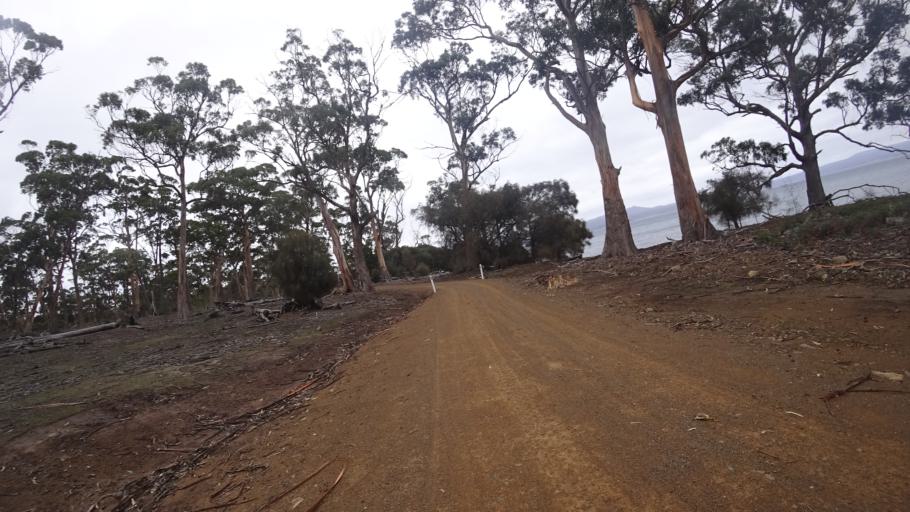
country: AU
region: Tasmania
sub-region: Sorell
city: Sorell
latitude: -42.6078
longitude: 148.0486
